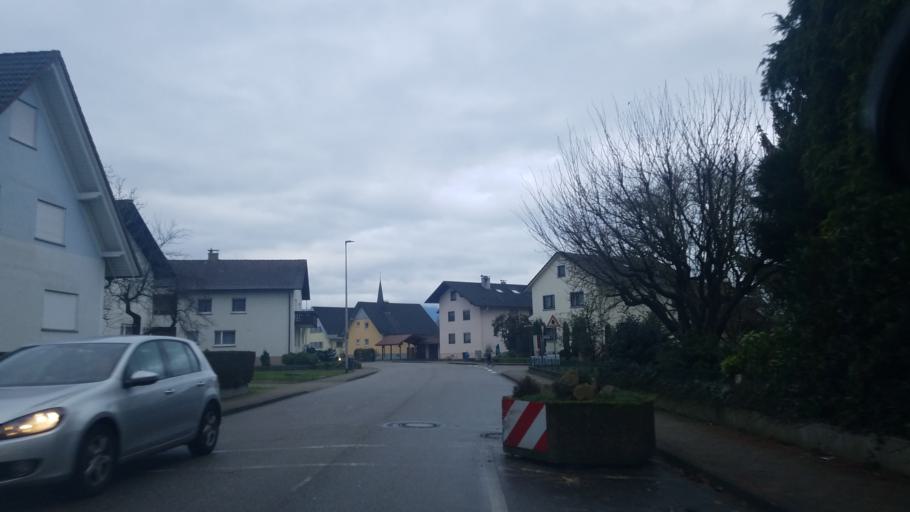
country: DE
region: Baden-Wuerttemberg
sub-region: Karlsruhe Region
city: Ottenhofen
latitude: 48.7218
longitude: 8.1135
